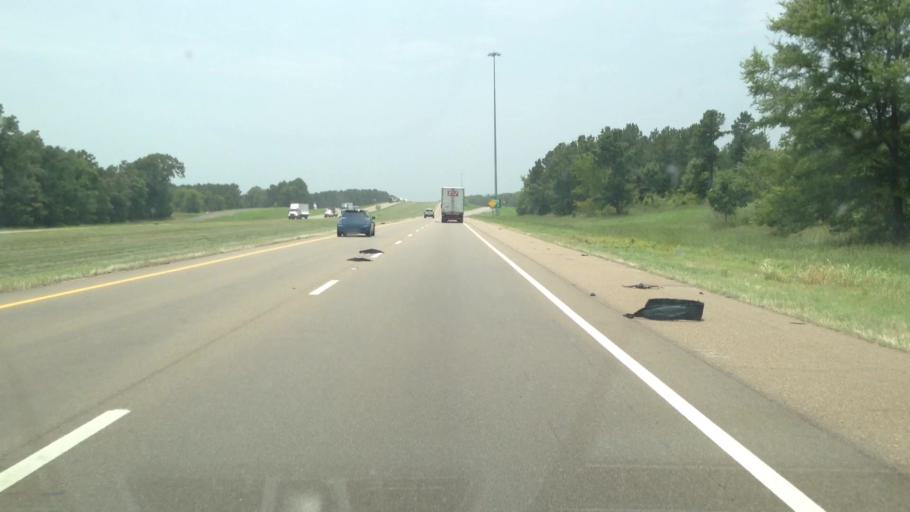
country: US
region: Texas
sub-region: Bowie County
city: De Kalb
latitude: 33.4205
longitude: -94.5516
